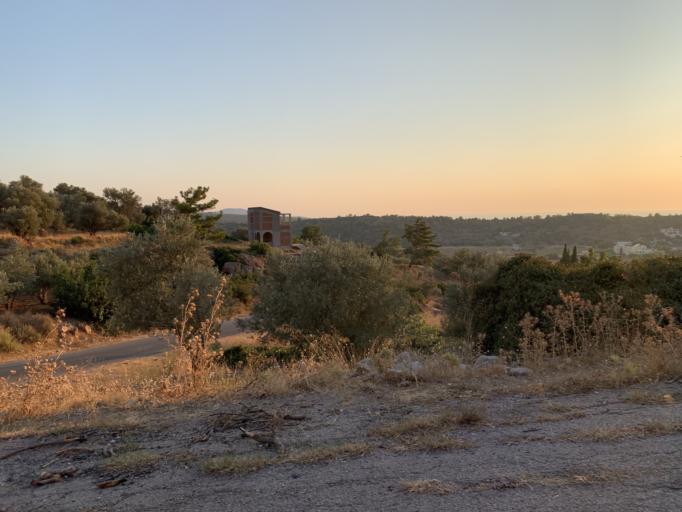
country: GR
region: North Aegean
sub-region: Chios
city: Thymiana
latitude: 38.3403
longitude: 25.9999
